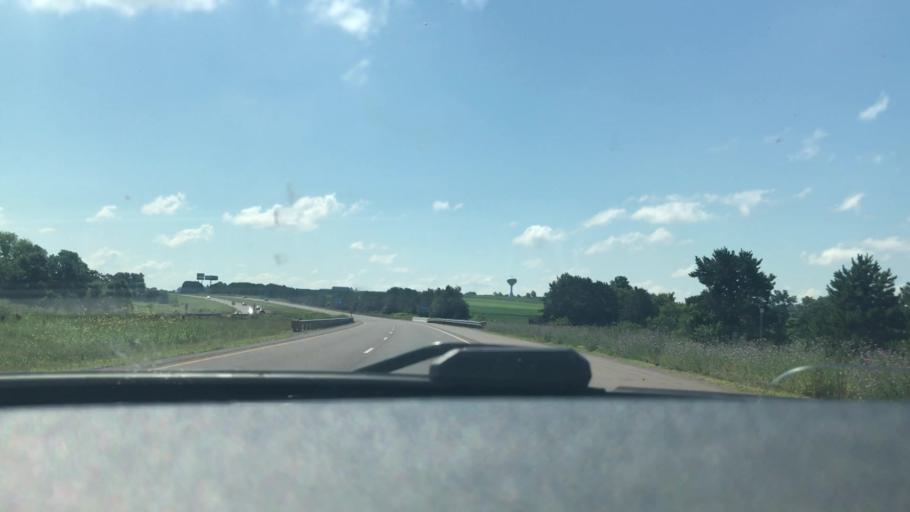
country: US
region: Wisconsin
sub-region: Chippewa County
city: Bloomer
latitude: 45.1104
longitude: -91.5170
